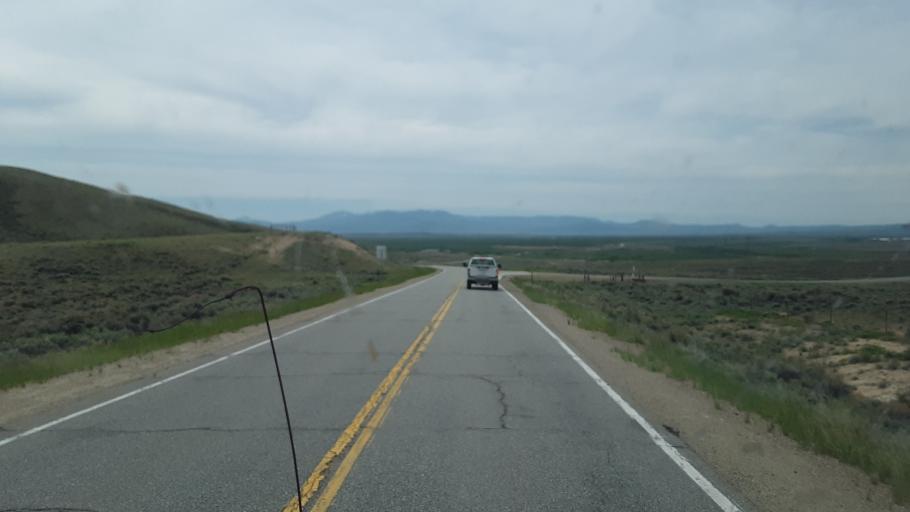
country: US
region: Colorado
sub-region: Jackson County
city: Walden
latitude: 40.6527
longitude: -106.3974
